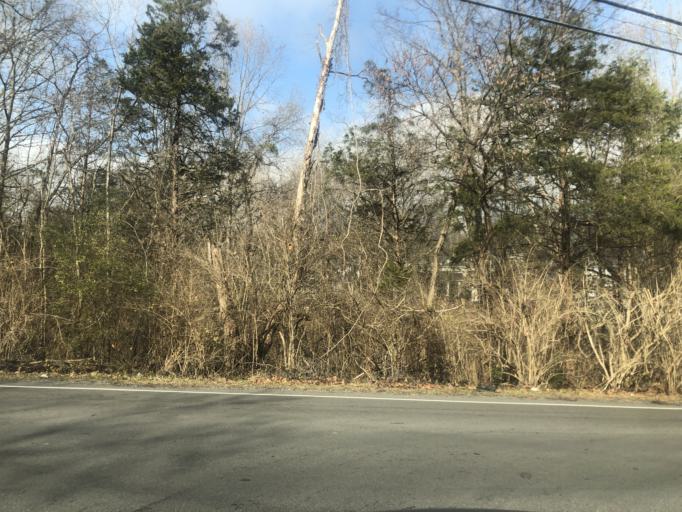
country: US
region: Tennessee
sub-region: Rutherford County
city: La Vergne
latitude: 36.0759
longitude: -86.6599
